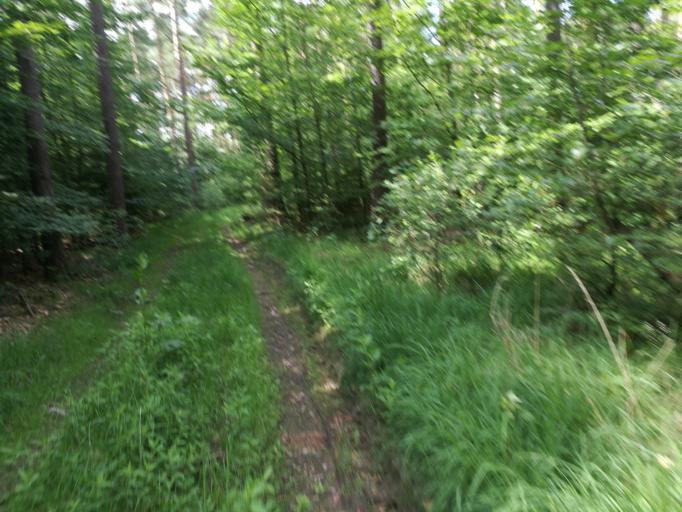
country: DE
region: Bavaria
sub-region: Regierungsbezirk Mittelfranken
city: Seukendorf
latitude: 49.4971
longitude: 10.8875
